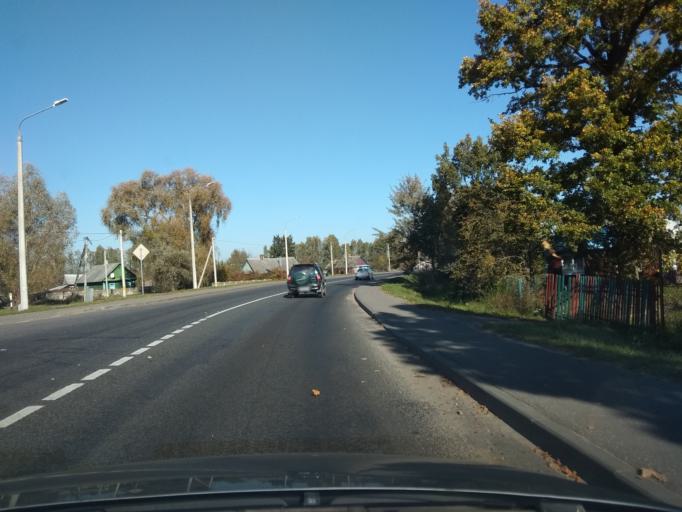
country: BY
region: Brest
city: Kobryn
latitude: 52.1587
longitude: 24.3078
